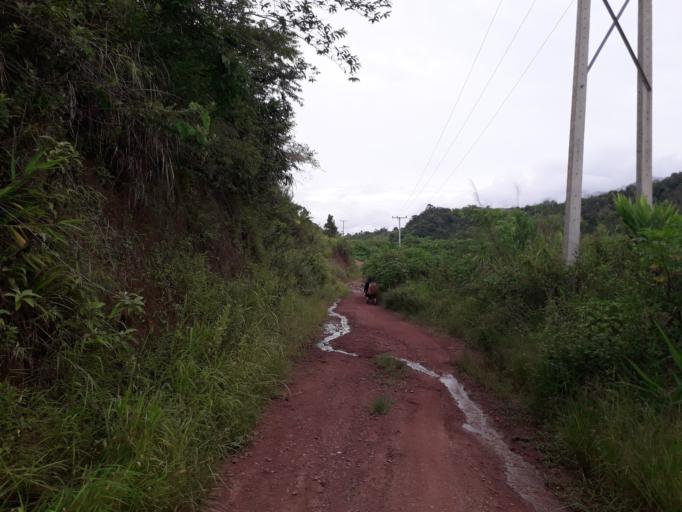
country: CN
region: Yunnan
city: Menglie
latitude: 22.2569
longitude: 101.5984
